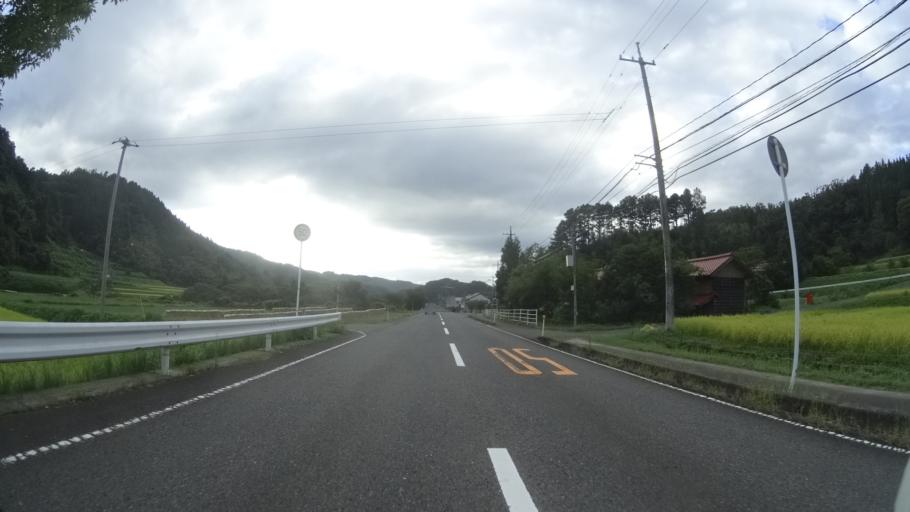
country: JP
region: Tottori
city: Kurayoshi
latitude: 35.4113
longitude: 133.9236
